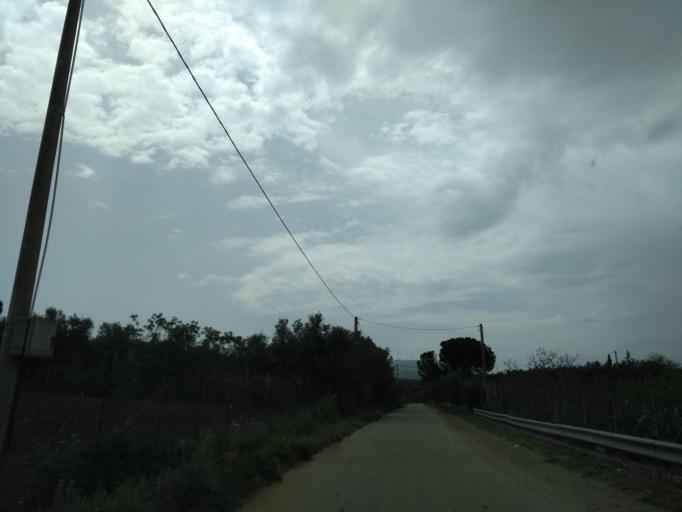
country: IT
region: Sicily
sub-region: Palermo
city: Partinico
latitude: 37.9936
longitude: 13.0762
